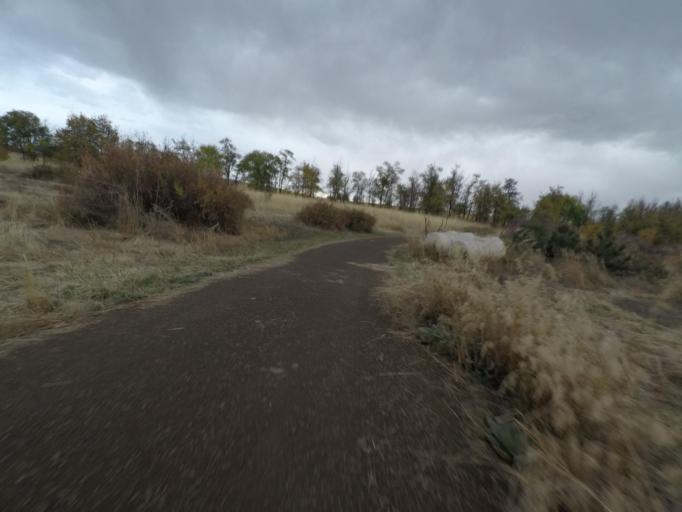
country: US
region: Washington
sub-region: Walla Walla County
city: Walla Walla East
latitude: 46.0737
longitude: -118.2572
